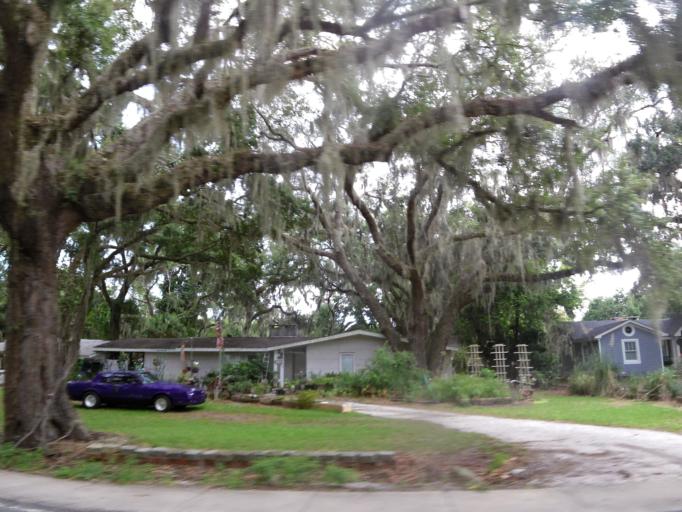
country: US
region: Georgia
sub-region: Glynn County
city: Saint Simons Island
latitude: 31.1574
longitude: -81.3819
